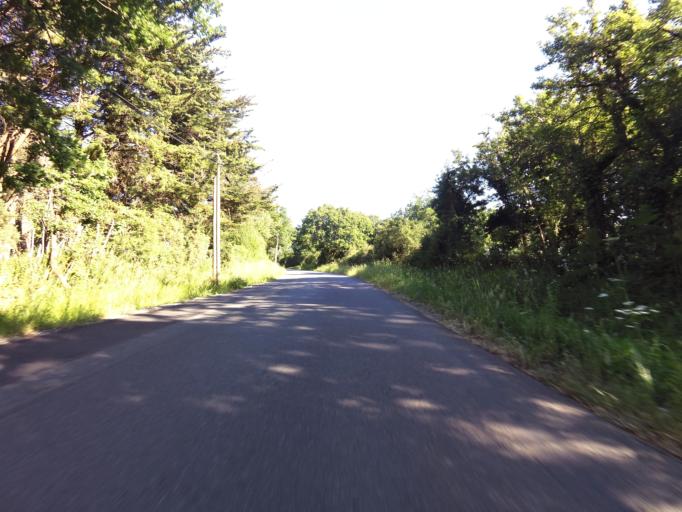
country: FR
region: Brittany
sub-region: Departement du Morbihan
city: Penestin
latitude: 47.4722
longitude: -2.4602
